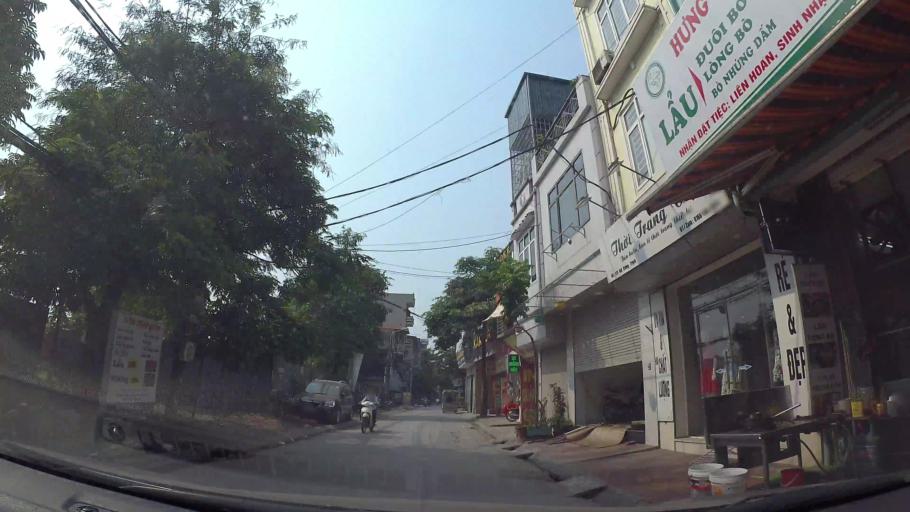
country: VN
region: Ha Noi
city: Thanh Xuan
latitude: 20.9865
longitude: 105.8190
